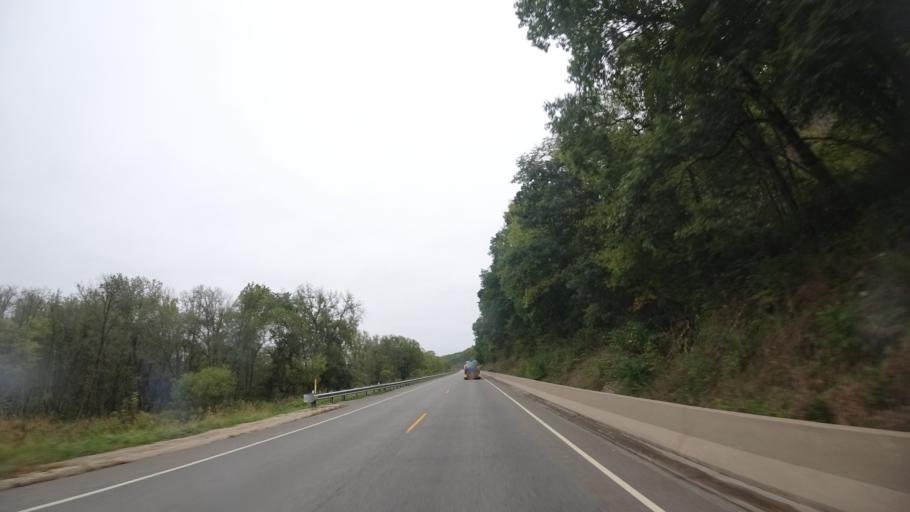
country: US
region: Wisconsin
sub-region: Crawford County
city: Prairie du Chien
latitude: 43.0740
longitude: -90.9378
